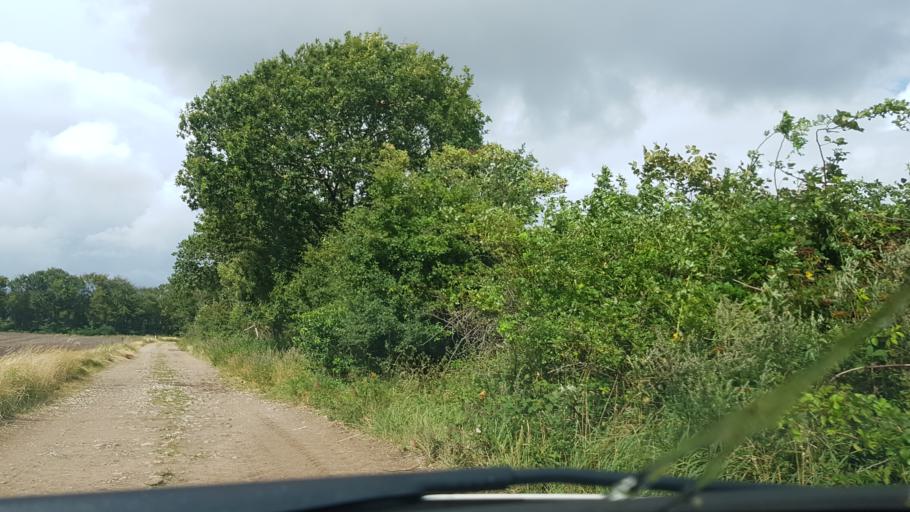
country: DK
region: South Denmark
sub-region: Esbjerg Kommune
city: Ribe
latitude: 55.2594
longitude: 8.7584
